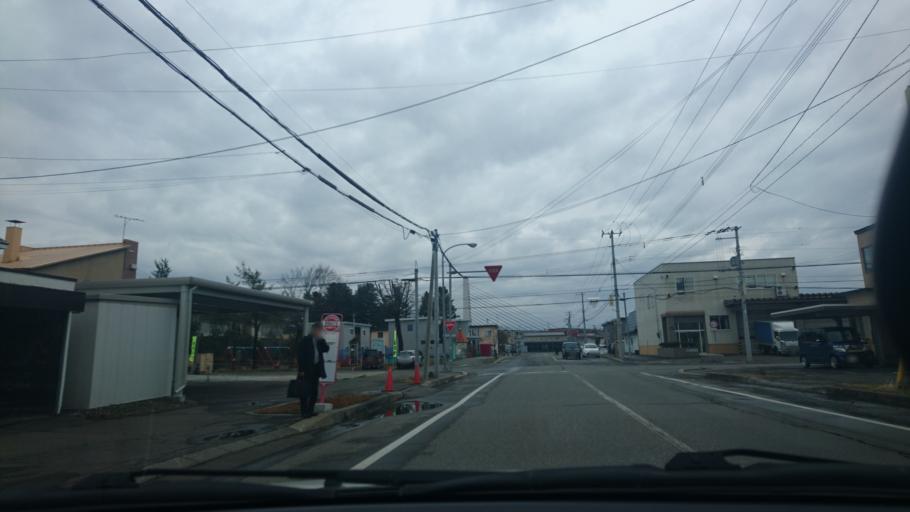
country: JP
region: Hokkaido
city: Obihiro
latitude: 42.9350
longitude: 143.1952
